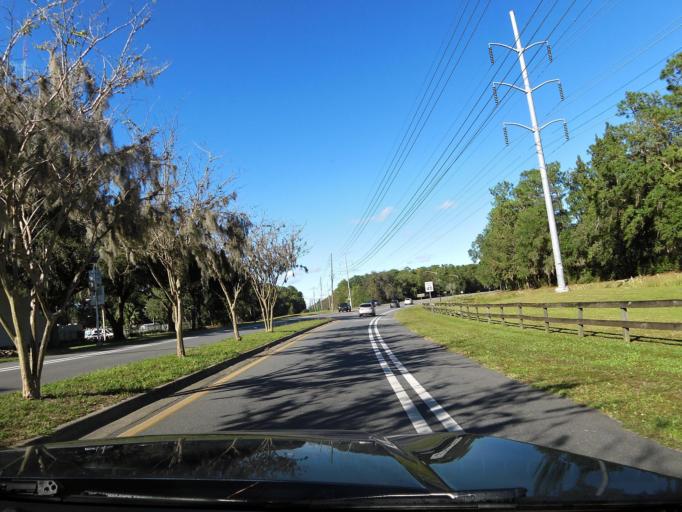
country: US
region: Florida
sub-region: Alachua County
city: Alachua
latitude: 29.7096
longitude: -82.3890
